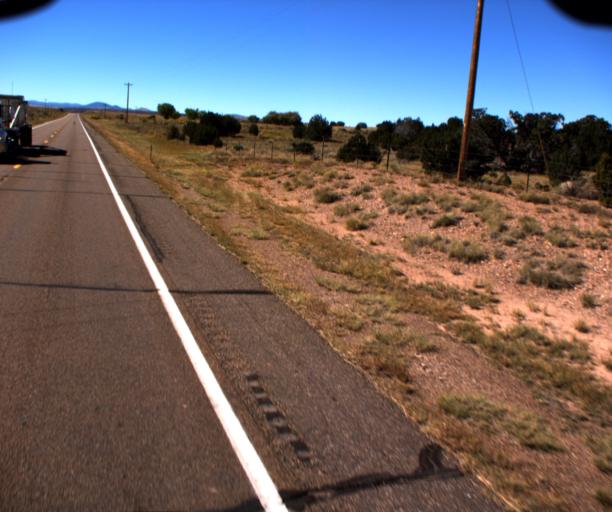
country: US
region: Arizona
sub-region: Apache County
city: Saint Johns
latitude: 34.4677
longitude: -109.3950
